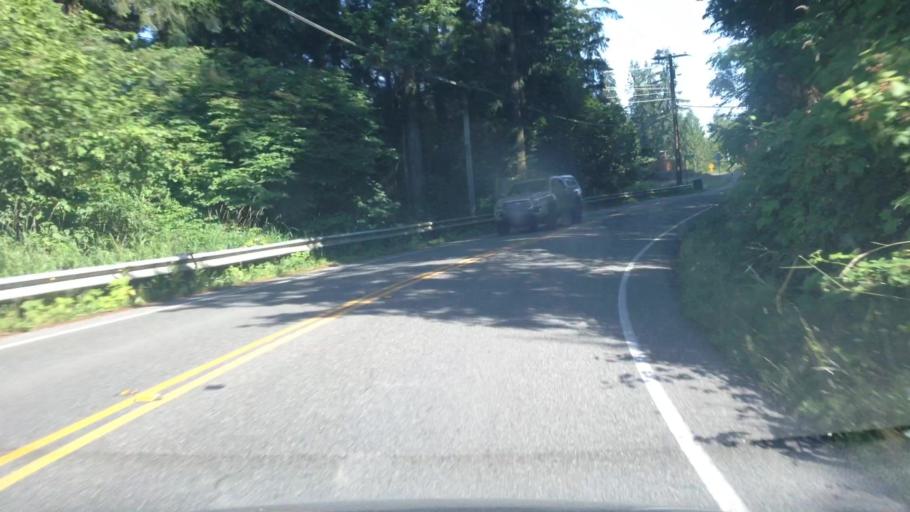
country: US
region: Washington
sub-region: King County
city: Lake Marcel-Stillwater
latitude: 47.7459
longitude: -121.9287
